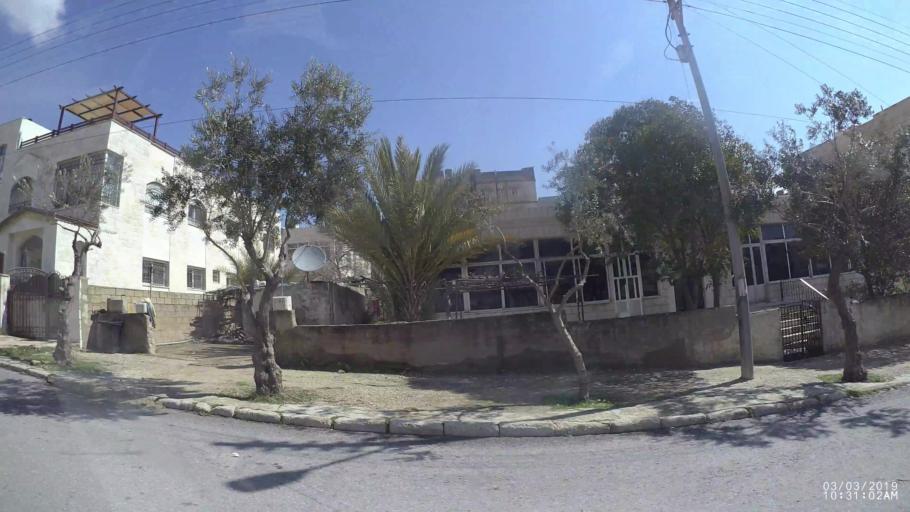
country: JO
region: Amman
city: Al Jubayhah
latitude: 31.9951
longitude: 35.9029
